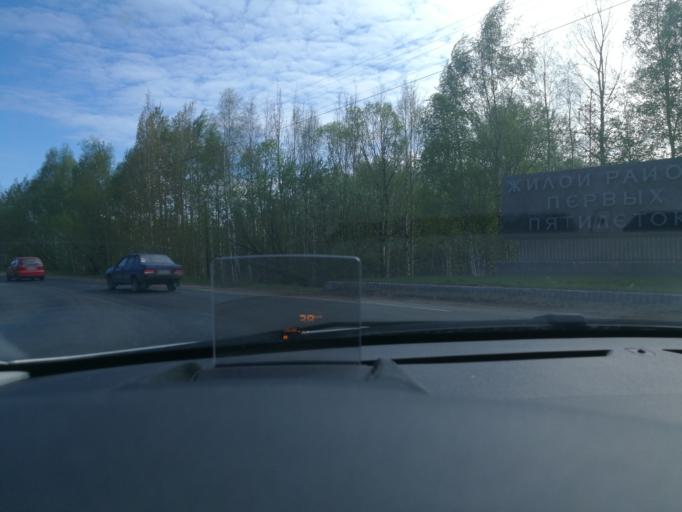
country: RU
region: Arkhangelskaya
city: Arkhangel'sk
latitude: 64.5956
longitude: 40.5473
